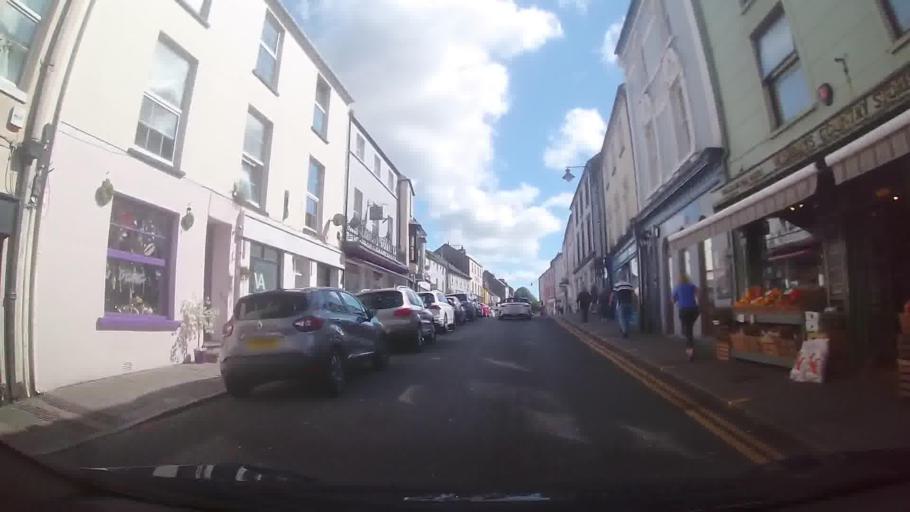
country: GB
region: Wales
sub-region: Pembrokeshire
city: Pembroke
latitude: 51.6759
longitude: -4.9175
